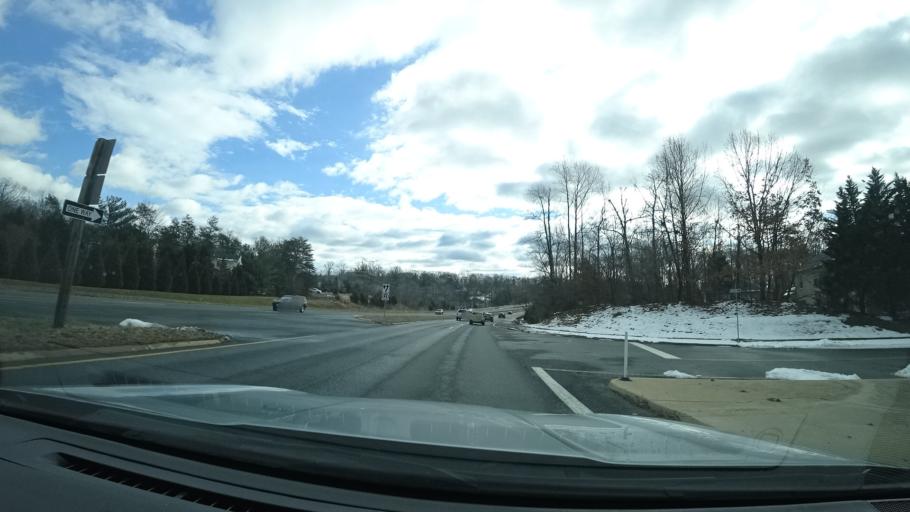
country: US
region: Virginia
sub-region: Fairfax County
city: Dranesville
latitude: 38.9894
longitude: -77.3614
